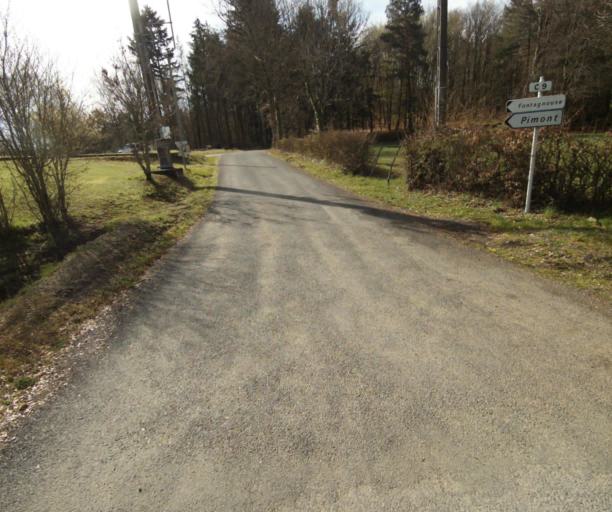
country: FR
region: Limousin
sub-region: Departement de la Correze
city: Laguenne
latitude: 45.2789
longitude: 1.8381
